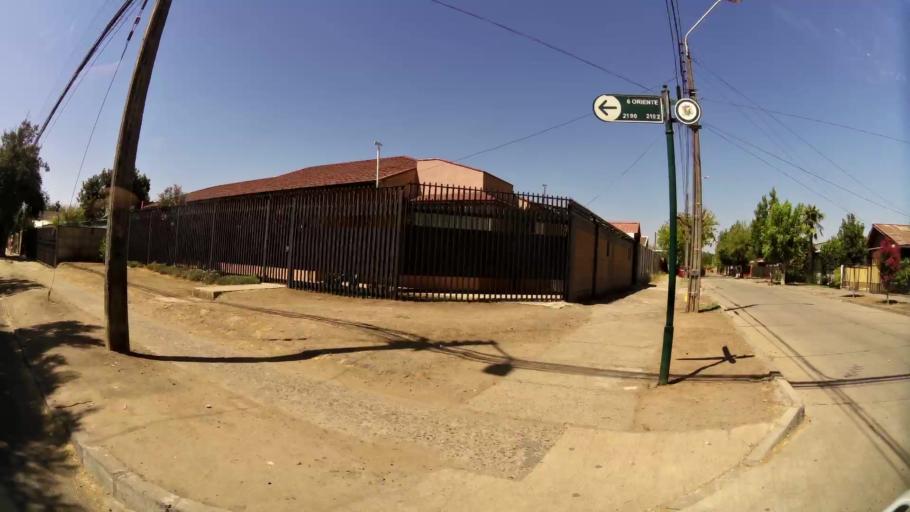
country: CL
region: Maule
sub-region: Provincia de Talca
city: Talca
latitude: -35.4146
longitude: -71.6574
